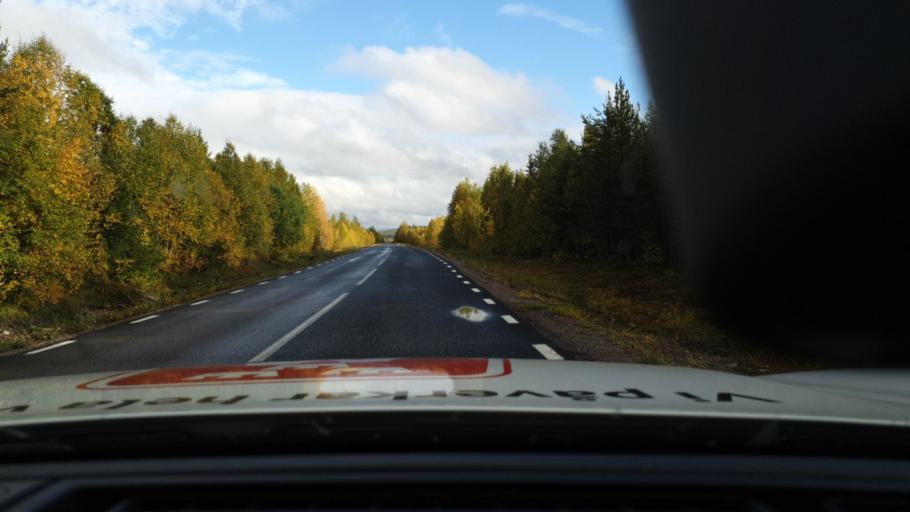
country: SE
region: Norrbotten
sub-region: Overkalix Kommun
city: OEverkalix
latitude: 66.9231
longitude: 22.7440
